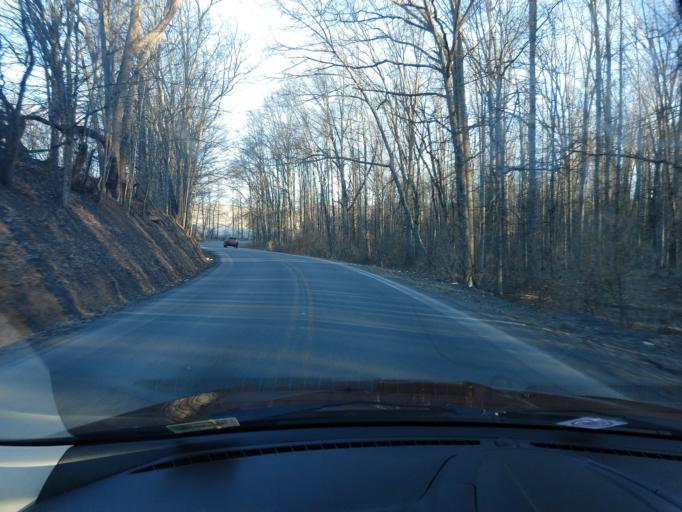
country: US
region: West Virginia
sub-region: Greenbrier County
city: Rainelle
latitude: 37.8604
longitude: -80.7186
